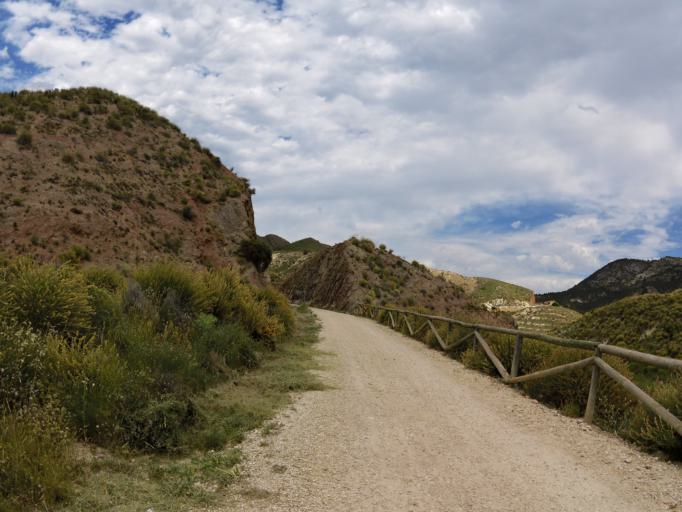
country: ES
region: Valencia
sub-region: Provincia de Alicante
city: Agost
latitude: 38.4792
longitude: -0.6373
